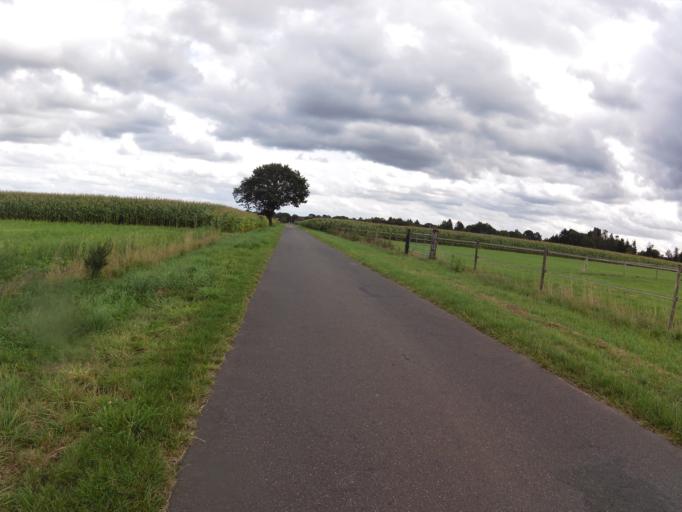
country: DE
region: Lower Saxony
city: Kohlen
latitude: 53.5121
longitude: 8.8516
